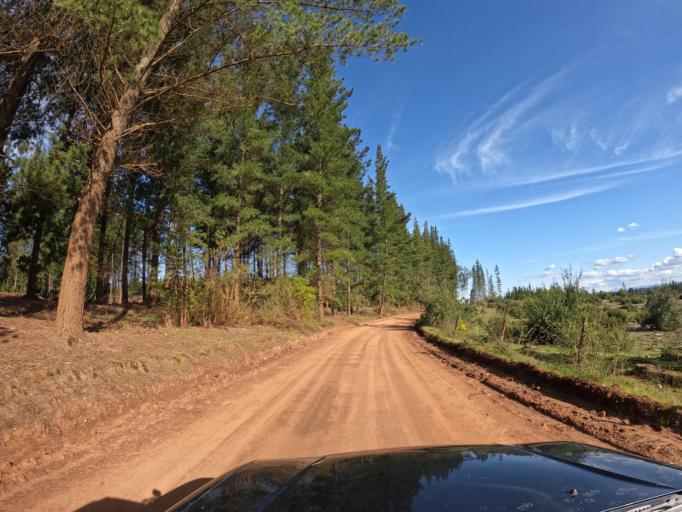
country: CL
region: Biobio
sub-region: Provincia de Biobio
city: La Laja
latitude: -37.1076
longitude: -72.7415
